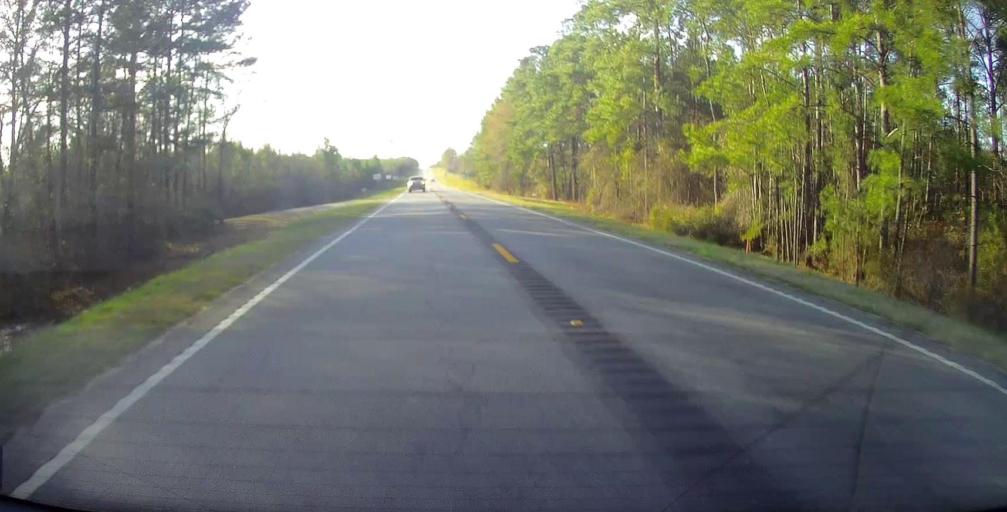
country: US
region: Georgia
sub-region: Tattnall County
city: Reidsville
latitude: 32.1204
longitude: -82.1959
